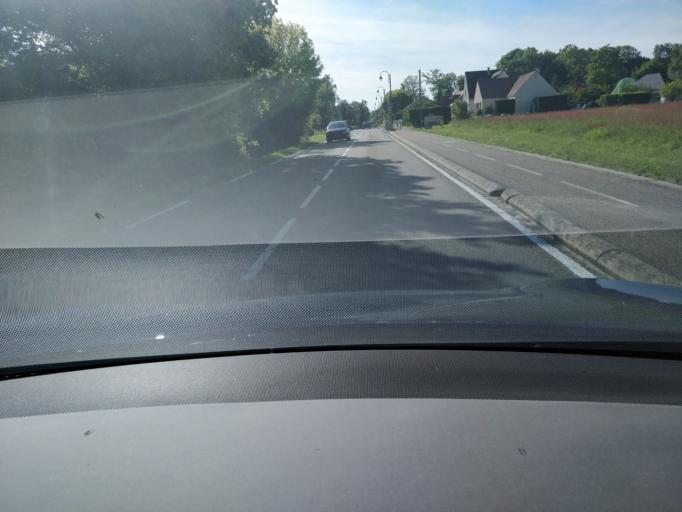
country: FR
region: Ile-de-France
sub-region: Departement de l'Essonne
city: Forges-les-Bains
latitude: 48.6260
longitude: 2.1105
